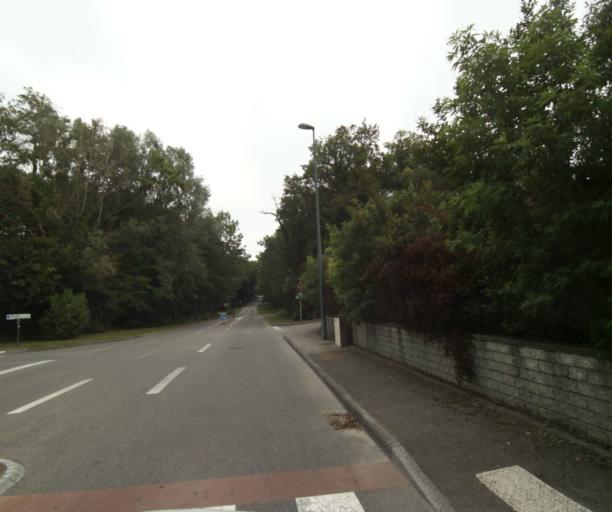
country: FR
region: Rhone-Alpes
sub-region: Departement de la Haute-Savoie
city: Sciez
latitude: 46.3253
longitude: 6.3935
